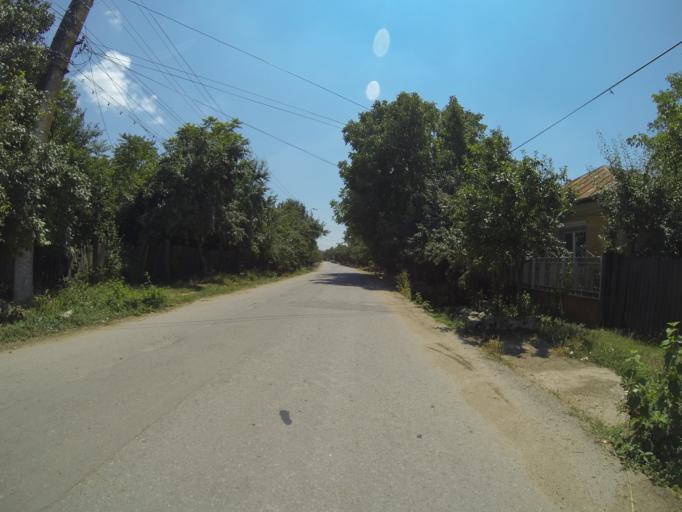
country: RO
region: Dolj
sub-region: Comuna Segarcea
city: Segarcea
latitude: 44.0898
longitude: 23.7467
